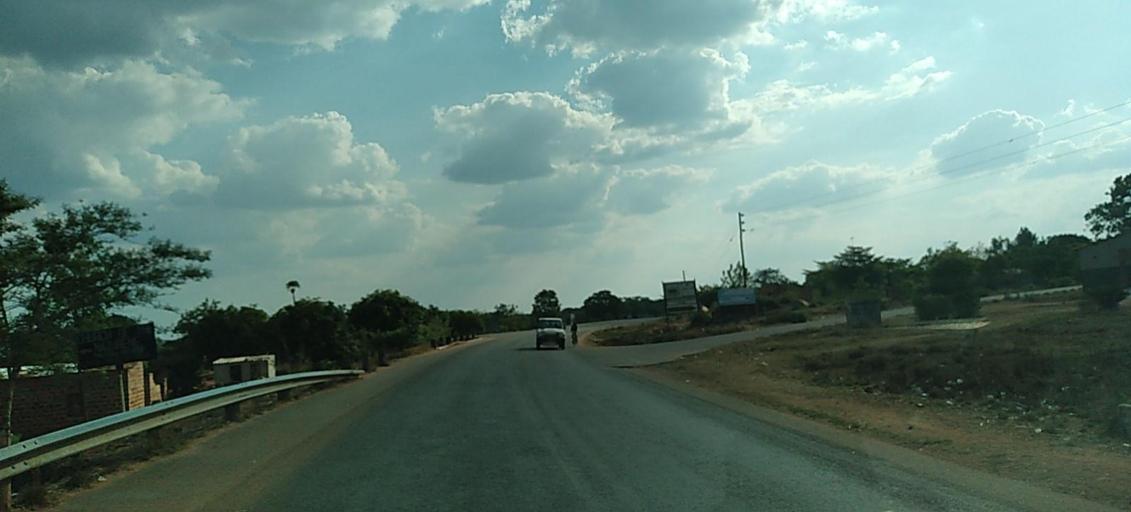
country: ZM
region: Copperbelt
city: Luanshya
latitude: -13.3612
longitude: 28.4133
